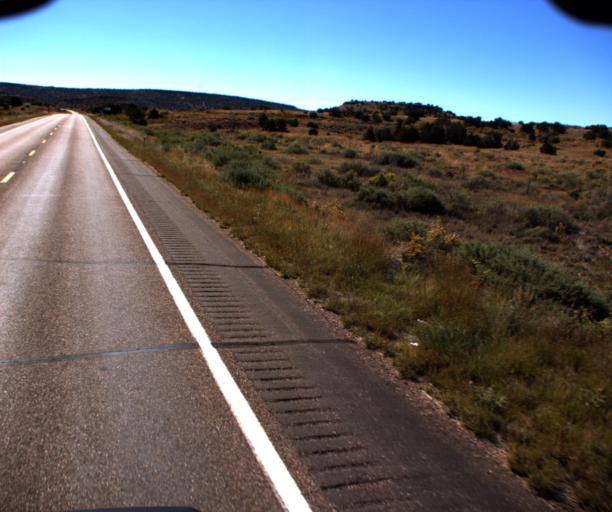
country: US
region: Arizona
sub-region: Apache County
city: Saint Johns
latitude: 34.3915
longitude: -109.4078
